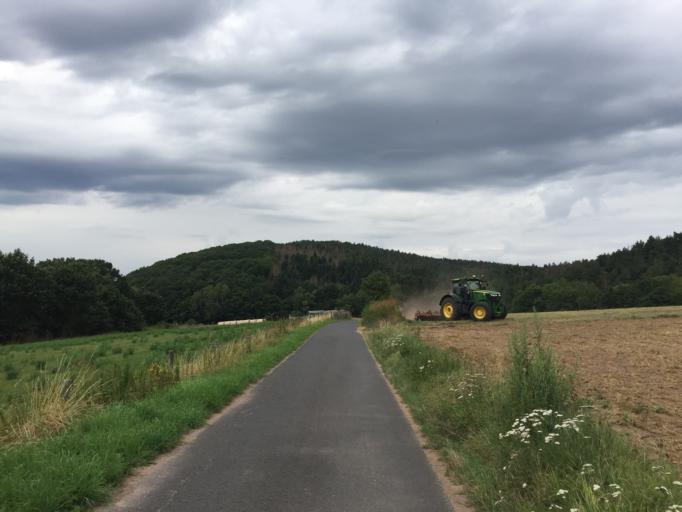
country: DE
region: Hesse
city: Breitenbach
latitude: 50.9327
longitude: 9.7910
